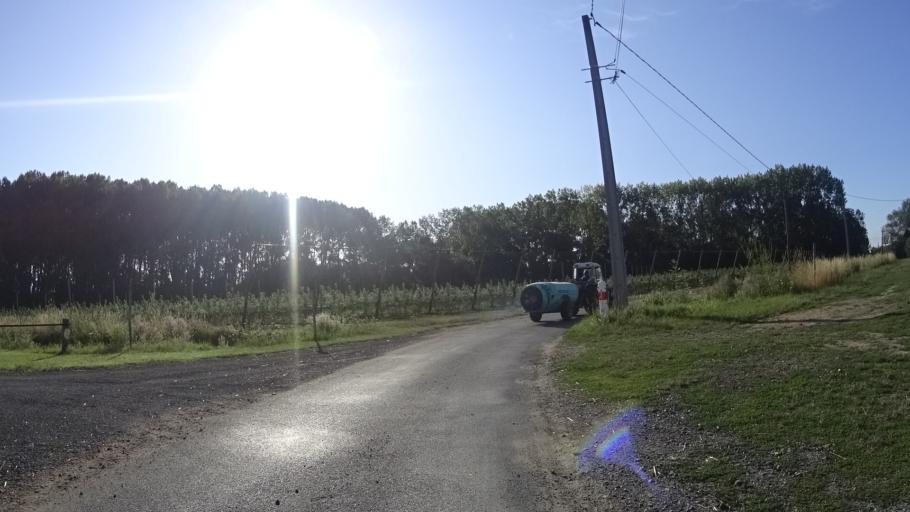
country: FR
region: Pays de la Loire
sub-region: Departement de Maine-et-Loire
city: Varennes-sur-Loire
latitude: 47.2585
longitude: 0.0276
